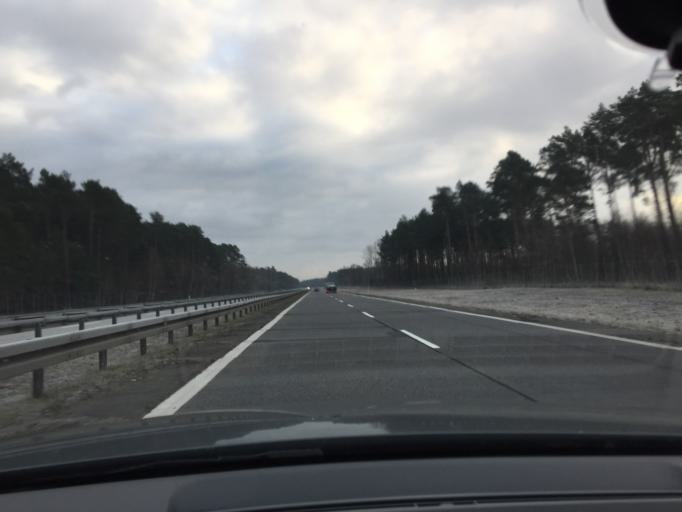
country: PL
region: Lubusz
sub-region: Powiat zarski
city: Trzebiel
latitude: 51.6199
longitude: 14.9052
